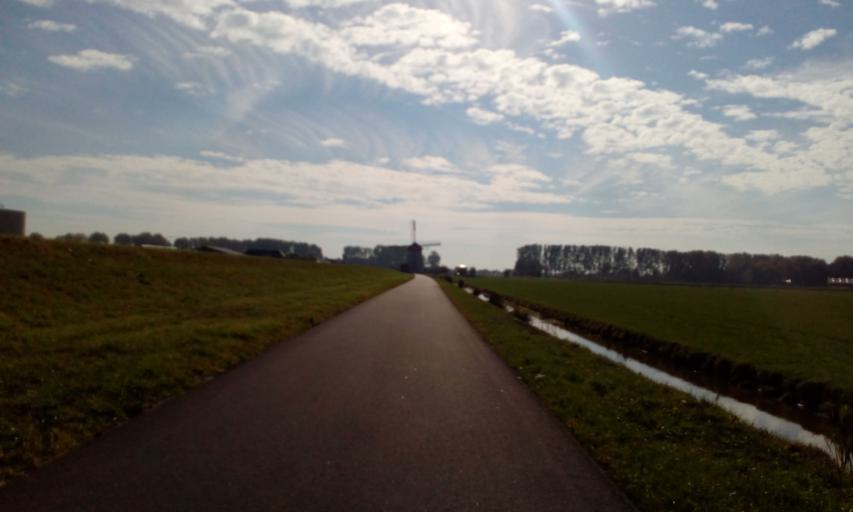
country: NL
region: South Holland
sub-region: Gemeente Westland
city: Kwintsheul
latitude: 51.9951
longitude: 4.2816
